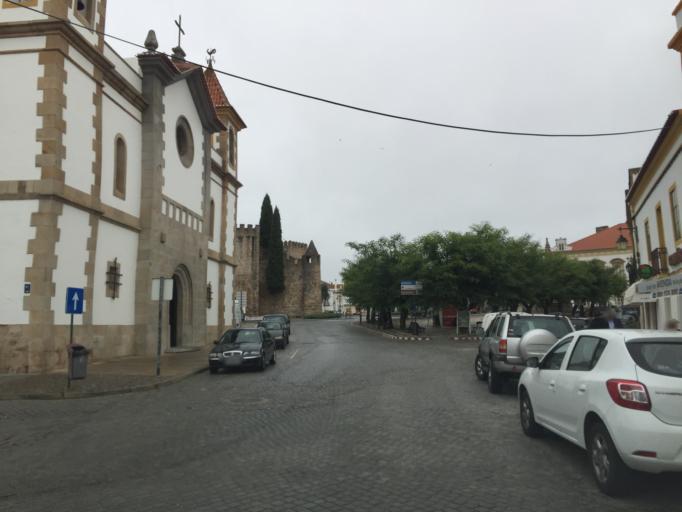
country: PT
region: Portalegre
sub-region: Alter do Chao
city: Alter do Chao
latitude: 39.1982
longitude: -7.6576
